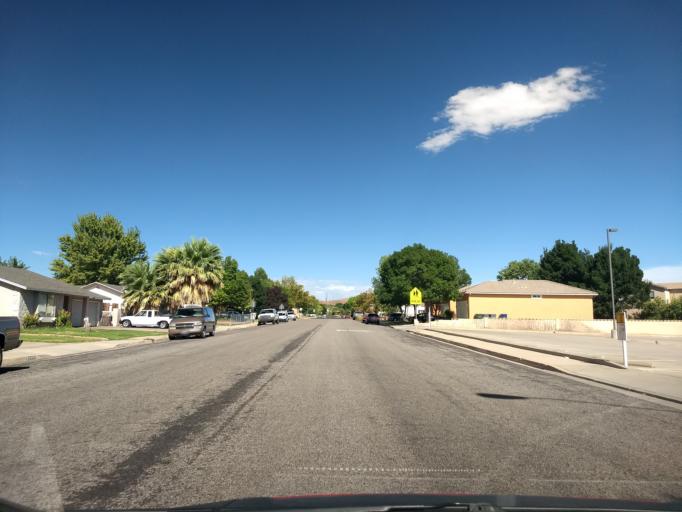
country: US
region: Utah
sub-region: Washington County
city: Santa Clara
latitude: 37.1294
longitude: -113.6207
